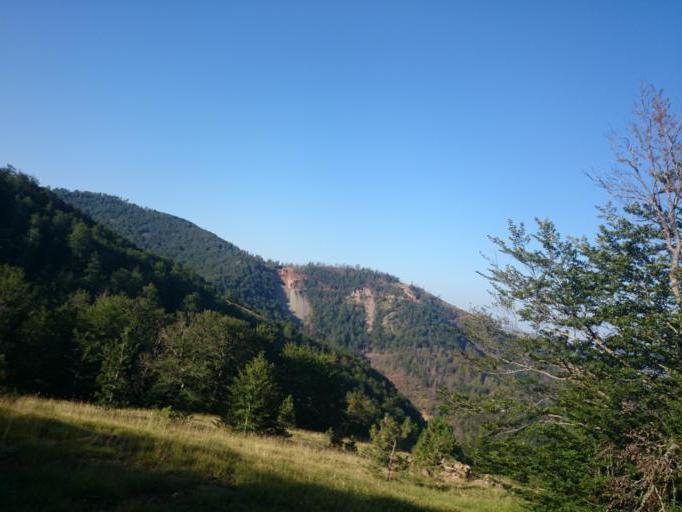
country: AL
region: Diber
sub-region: Rrethi i Bulqizes
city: Martanesh
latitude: 41.4048
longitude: 20.3038
